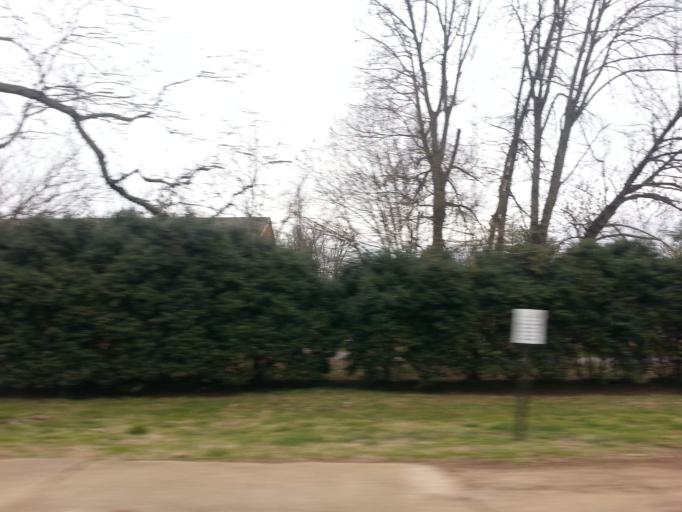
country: US
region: Tennessee
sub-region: Knox County
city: Knoxville
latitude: 35.9346
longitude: -83.9681
